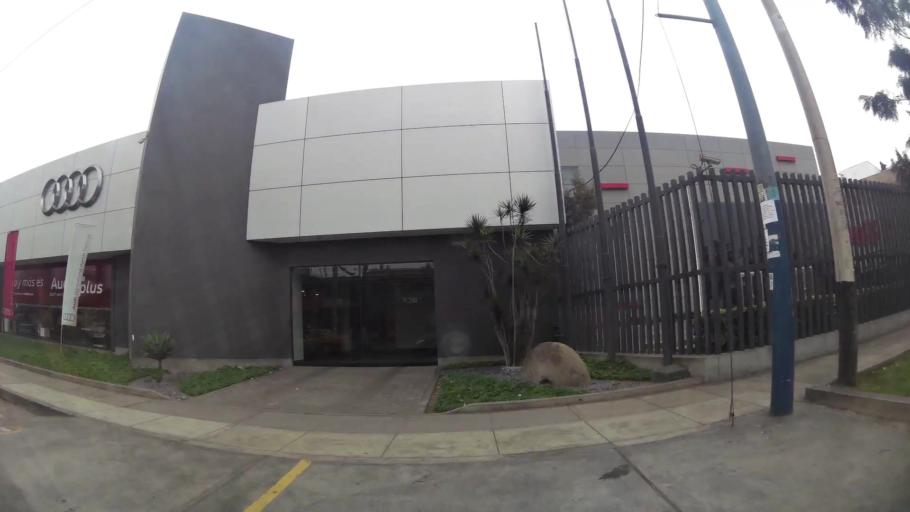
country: PE
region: Lima
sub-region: Lima
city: San Isidro
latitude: -12.1051
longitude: -77.0187
